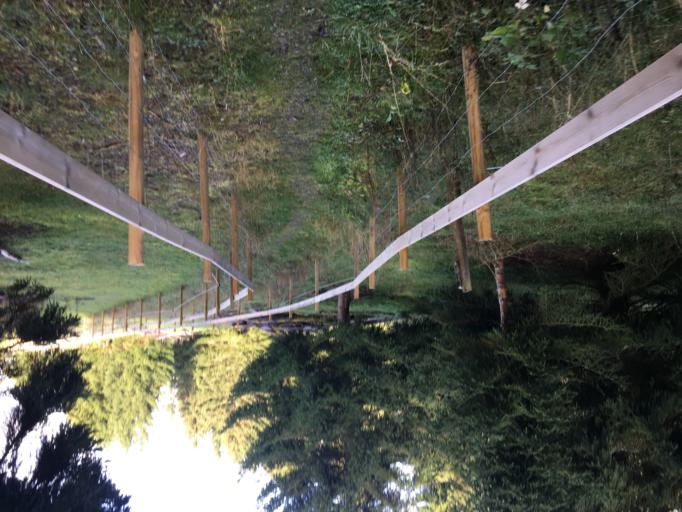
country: NO
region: Nord-Trondelag
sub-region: Leksvik
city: Leksvik
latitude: 63.5735
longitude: 10.6130
